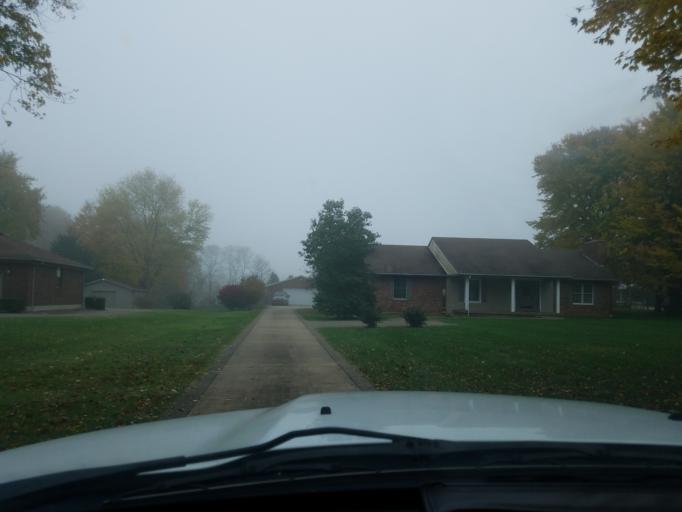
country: US
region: Indiana
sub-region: Floyd County
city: Georgetown
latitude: 38.3067
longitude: -85.9321
